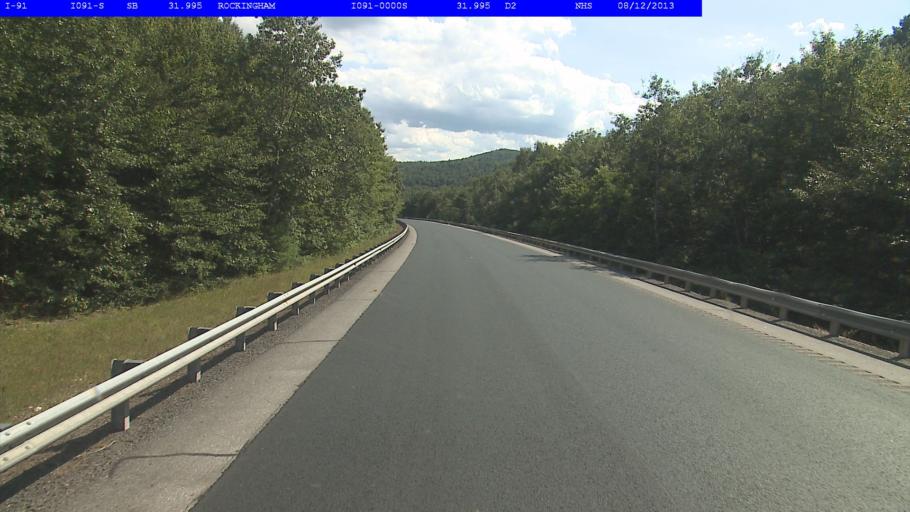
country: US
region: Vermont
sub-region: Windham County
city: Bellows Falls
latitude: 43.1352
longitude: -72.4773
